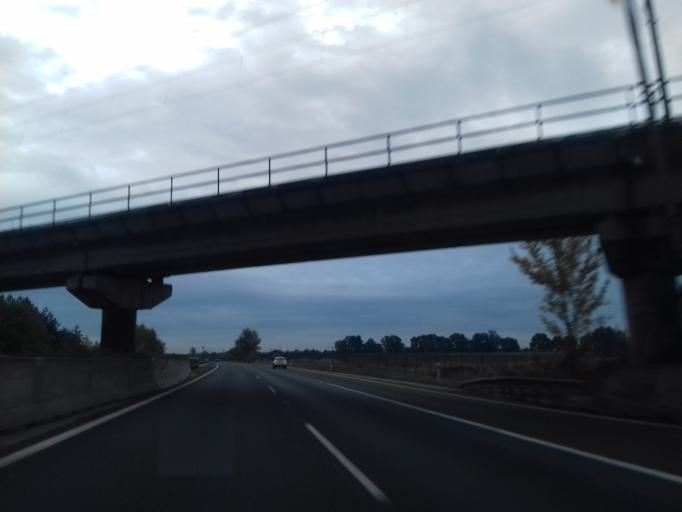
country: CZ
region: Central Bohemia
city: Poricany
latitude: 50.1184
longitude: 14.9448
